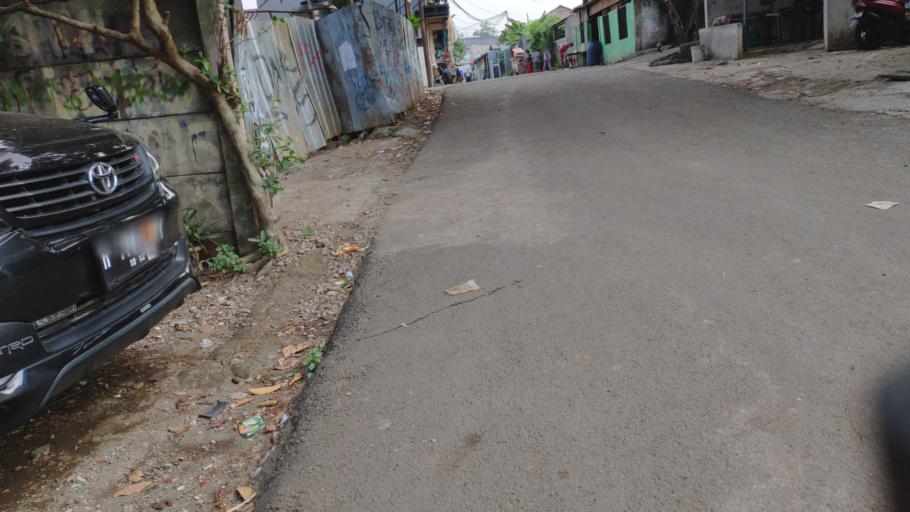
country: ID
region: West Java
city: Pamulang
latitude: -6.3124
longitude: 106.8070
